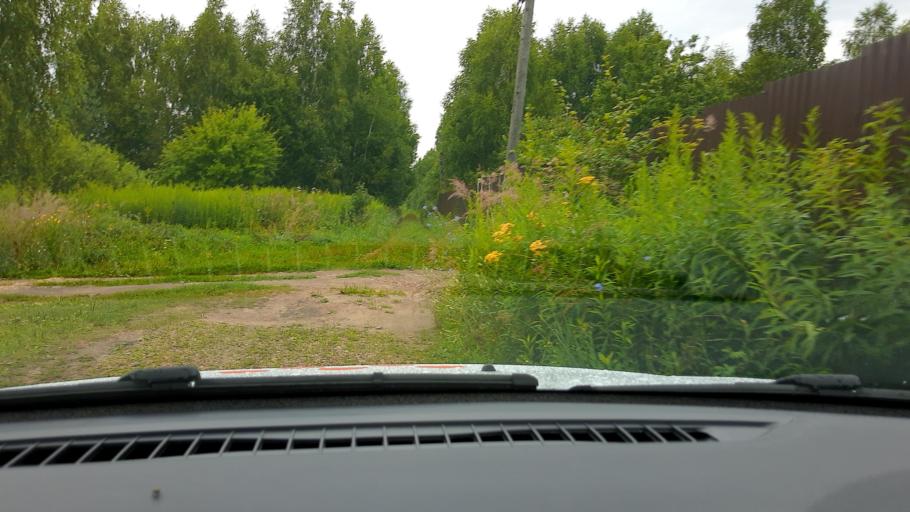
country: RU
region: Nizjnij Novgorod
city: Surovatikha
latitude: 55.9325
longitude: 43.9289
